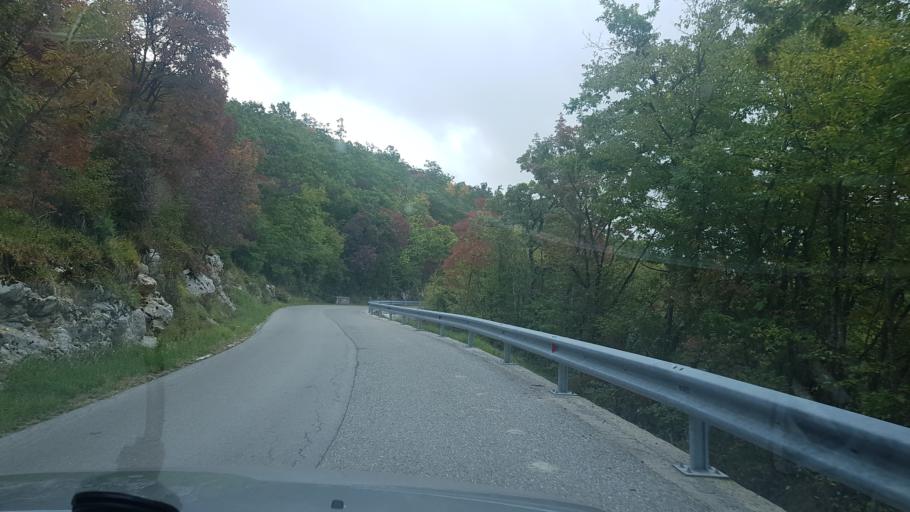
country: SI
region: Hrpelje-Kozina
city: Kozina
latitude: 45.5170
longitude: 13.9582
